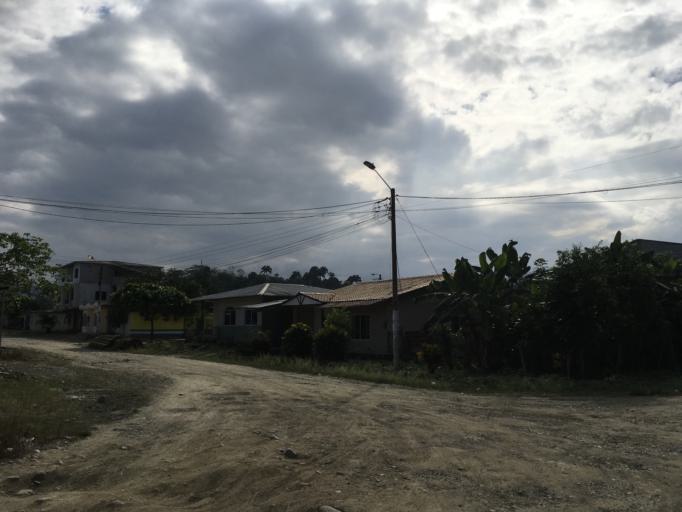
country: EC
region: Guayas
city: Balao
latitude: -2.9806
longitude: -79.6899
